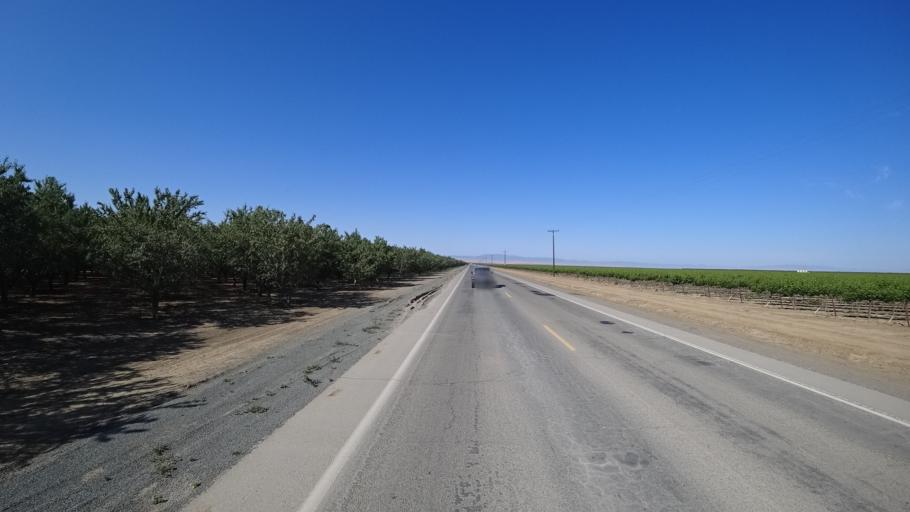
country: US
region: California
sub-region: Kings County
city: Lemoore Station
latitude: 36.1623
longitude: -119.9800
